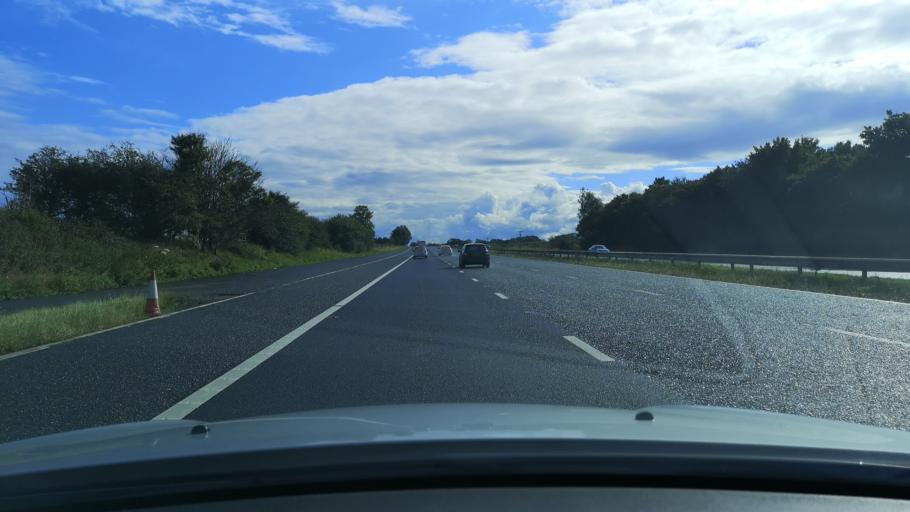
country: GB
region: England
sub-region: East Riding of Yorkshire
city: Pollington
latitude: 53.6907
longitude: -1.1079
